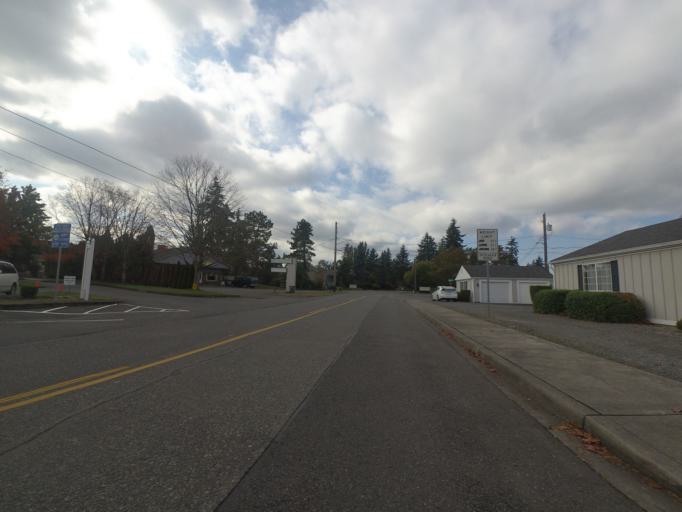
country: US
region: Washington
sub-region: Pierce County
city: Lakewood
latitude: 47.1704
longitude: -122.5229
